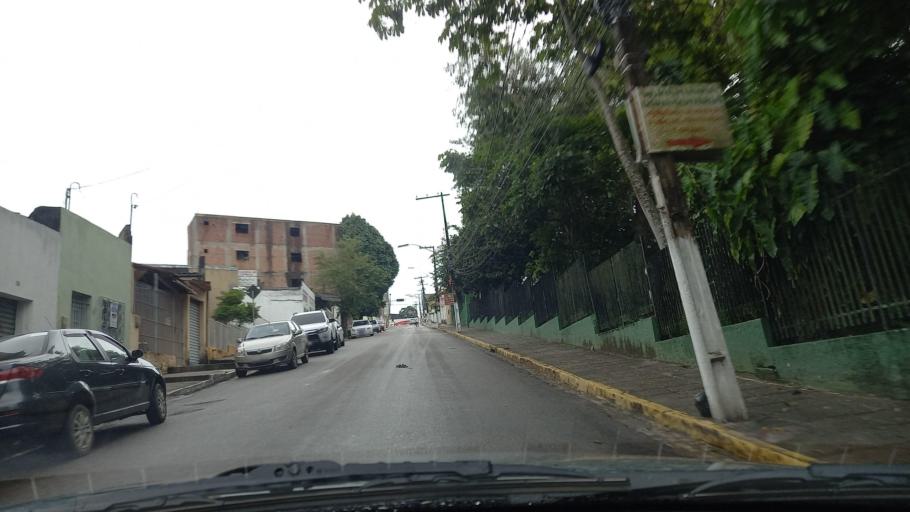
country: BR
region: Pernambuco
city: Garanhuns
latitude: -8.8934
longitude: -36.4915
